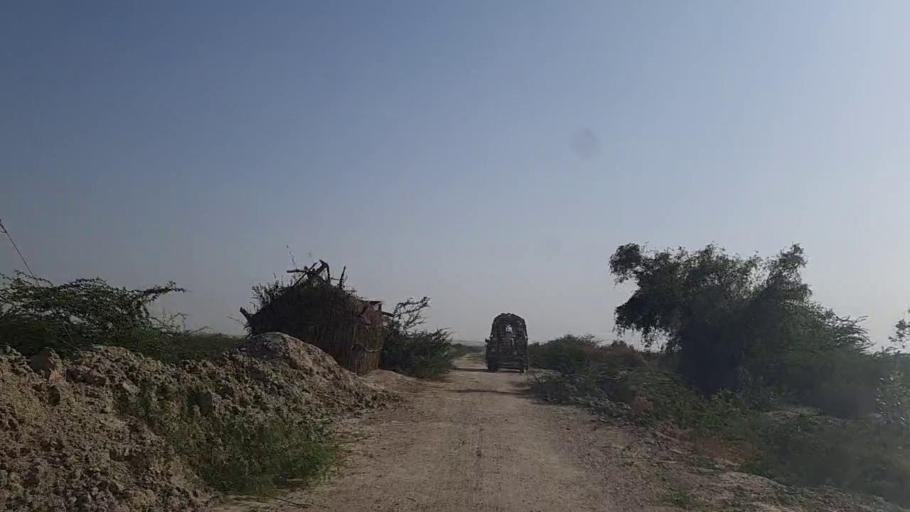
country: PK
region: Sindh
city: Kadhan
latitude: 24.5789
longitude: 69.2628
